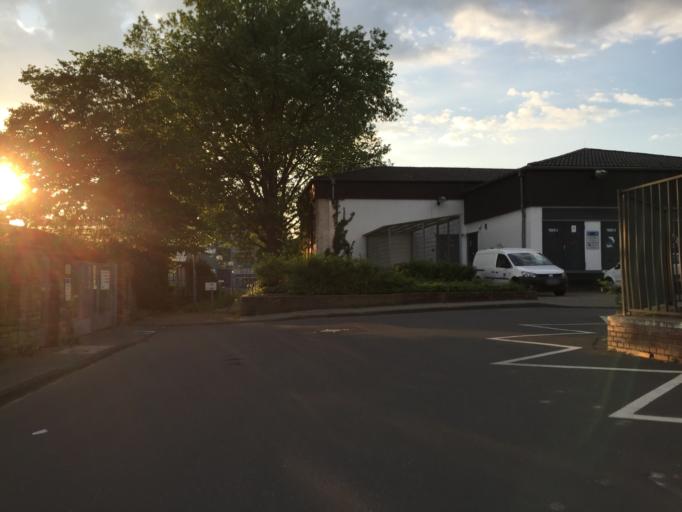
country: DE
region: North Rhine-Westphalia
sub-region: Regierungsbezirk Koln
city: Bonn
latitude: 50.7263
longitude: 7.0881
